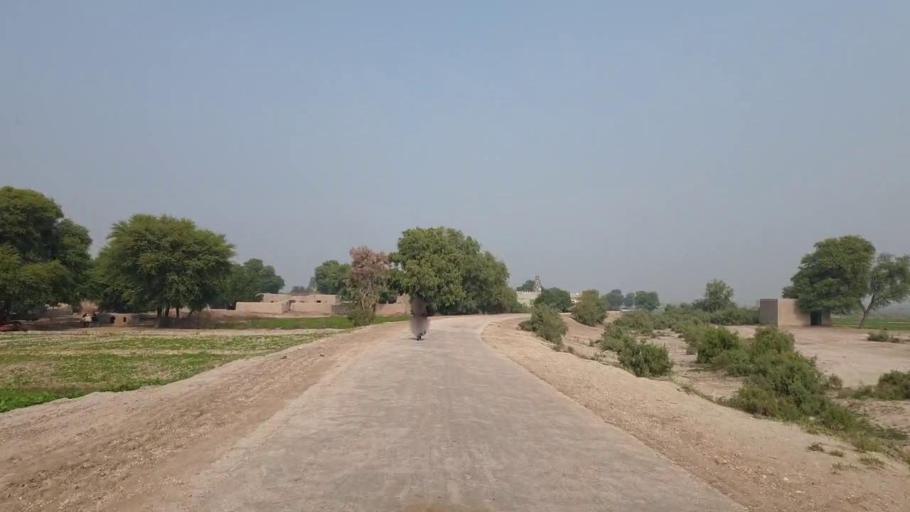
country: PK
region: Sindh
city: Bhan
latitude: 26.5229
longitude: 67.6910
